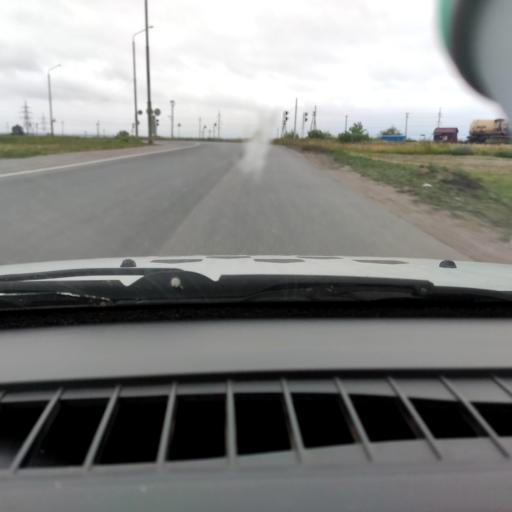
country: RU
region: Tatarstan
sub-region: Tukayevskiy Rayon
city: Naberezhnyye Chelny
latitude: 55.6694
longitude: 52.2746
